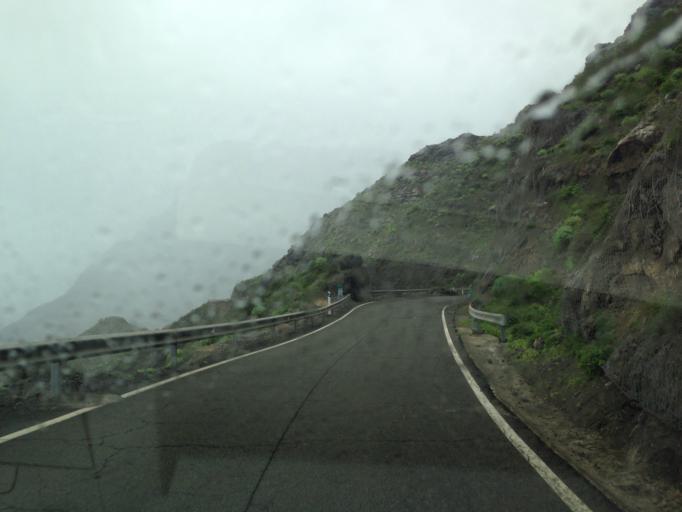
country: ES
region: Canary Islands
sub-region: Provincia de Las Palmas
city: San Nicolas
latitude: 28.0387
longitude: -15.7474
